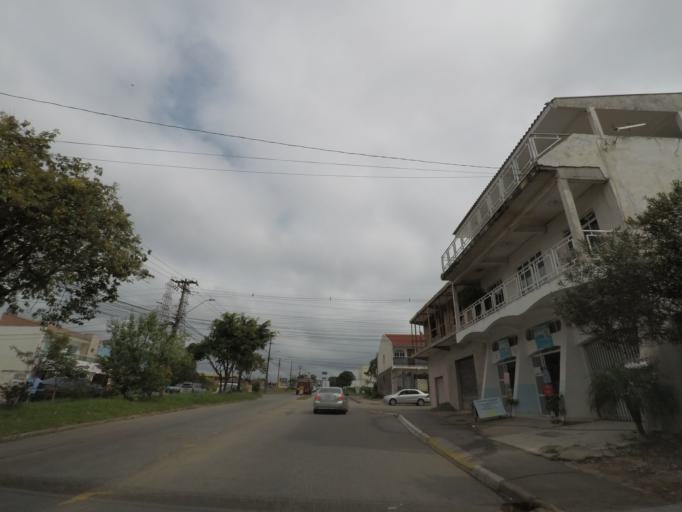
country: BR
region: Parana
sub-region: Curitiba
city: Curitiba
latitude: -25.4950
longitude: -49.3402
